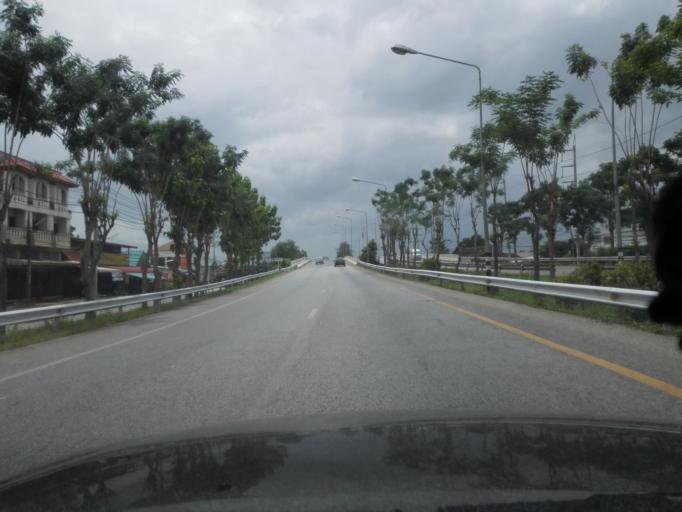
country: TH
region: Kamphaeng Phet
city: Kamphaeng Phet
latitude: 16.4807
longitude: 99.4947
